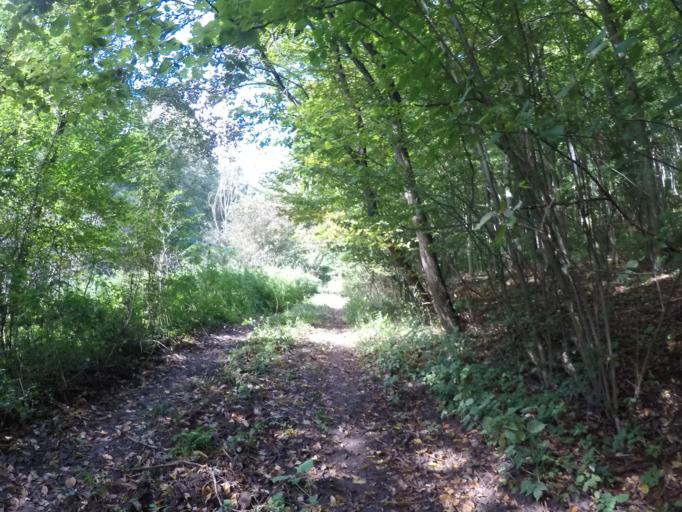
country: SK
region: Presovsky
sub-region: Okres Presov
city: Presov
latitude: 48.9372
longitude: 21.1492
